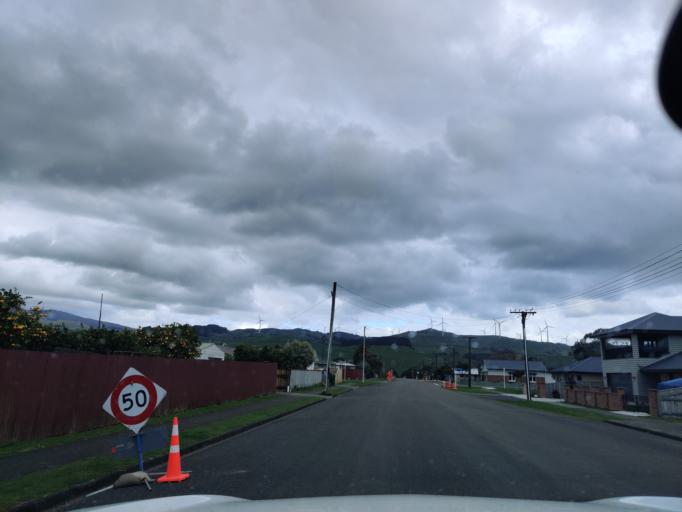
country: NZ
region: Manawatu-Wanganui
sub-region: Palmerston North City
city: Palmerston North
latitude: -40.2888
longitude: 175.7559
